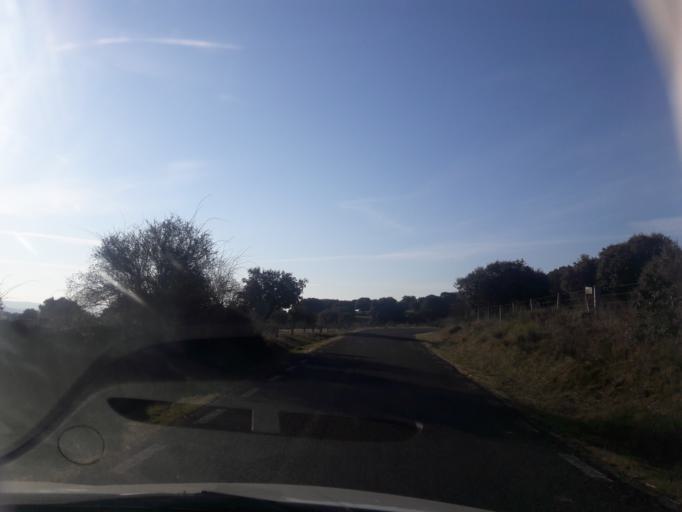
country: ES
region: Castille and Leon
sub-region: Provincia de Salamanca
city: Montejo
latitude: 40.6212
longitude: -5.6089
